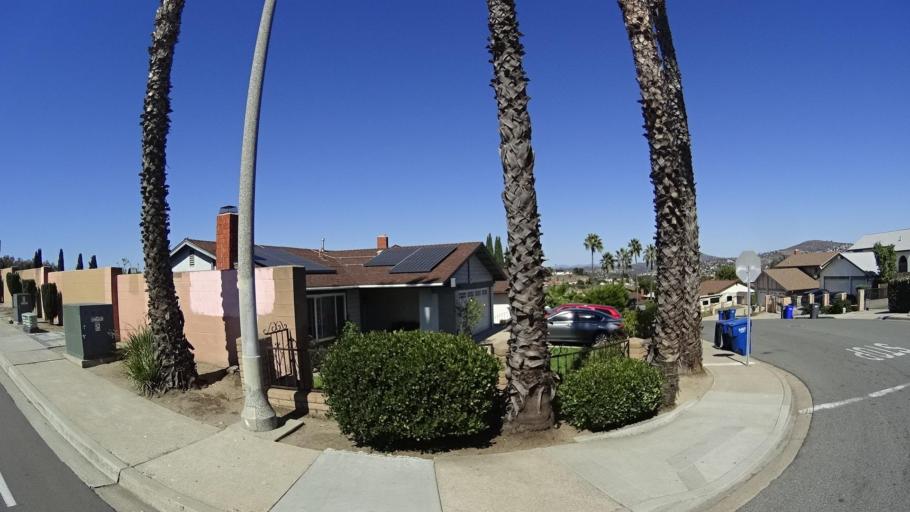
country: US
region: California
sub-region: San Diego County
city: La Presa
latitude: 32.6980
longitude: -117.0233
